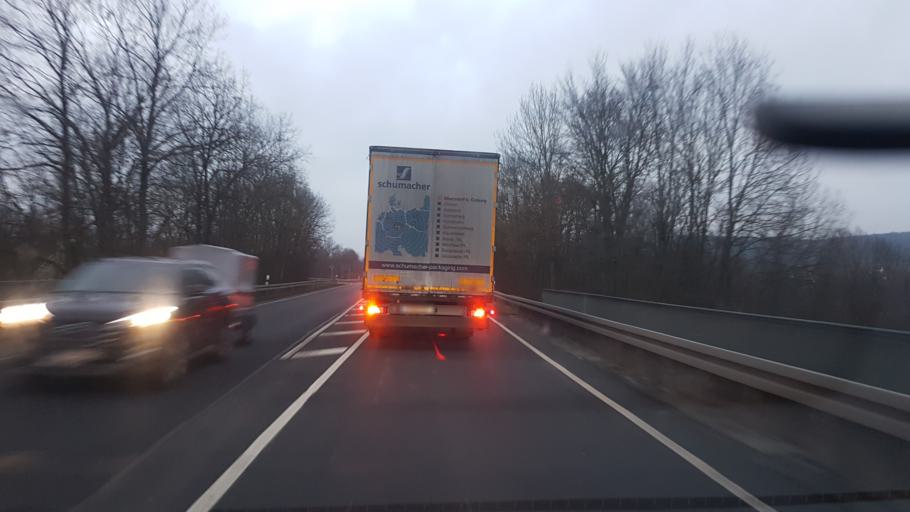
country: DE
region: Bavaria
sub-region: Regierungsbezirk Unterfranken
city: Rentweinsdorf
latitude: 50.0931
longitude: 10.7868
